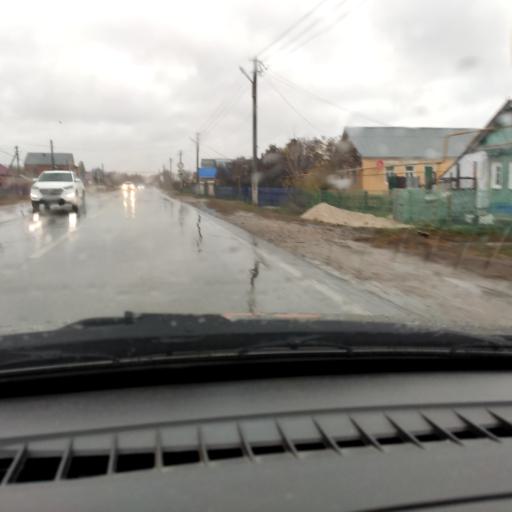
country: RU
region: Samara
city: Tol'yatti
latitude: 53.6480
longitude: 49.2931
